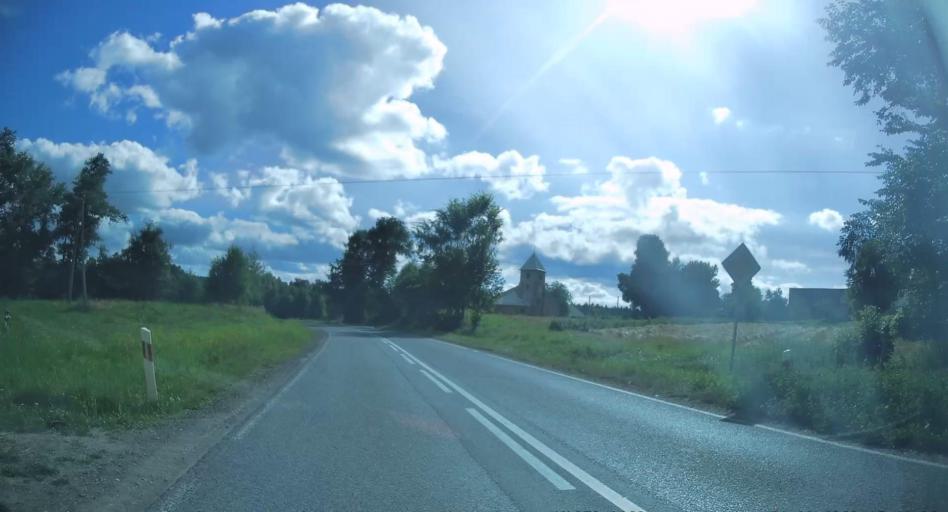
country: PL
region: Swietokrzyskie
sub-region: Powiat kielecki
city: Nowa Slupia
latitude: 50.8278
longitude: 21.0782
